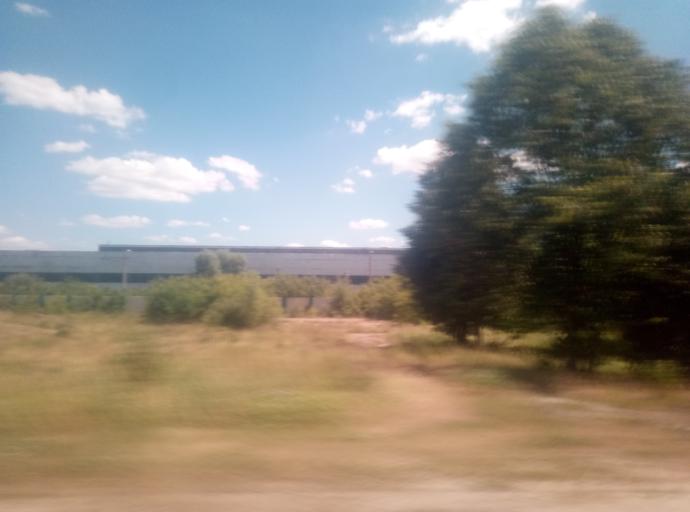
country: RU
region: Tula
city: Kireyevsk
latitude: 53.9585
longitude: 37.9382
